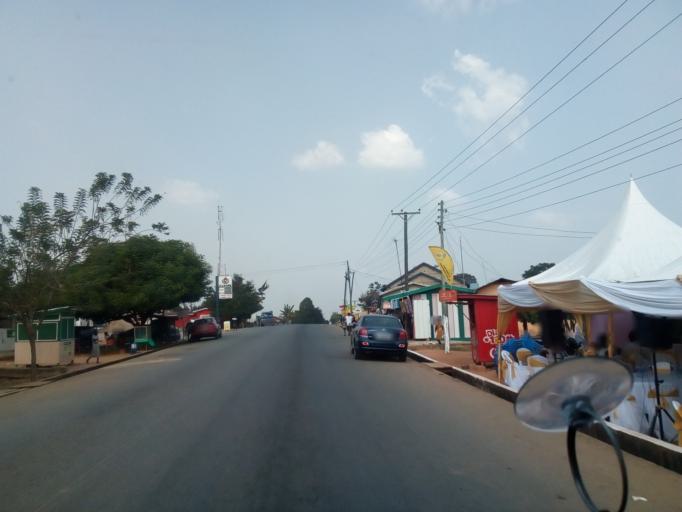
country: GH
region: Eastern
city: Suhum
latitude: 6.0456
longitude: -0.4126
